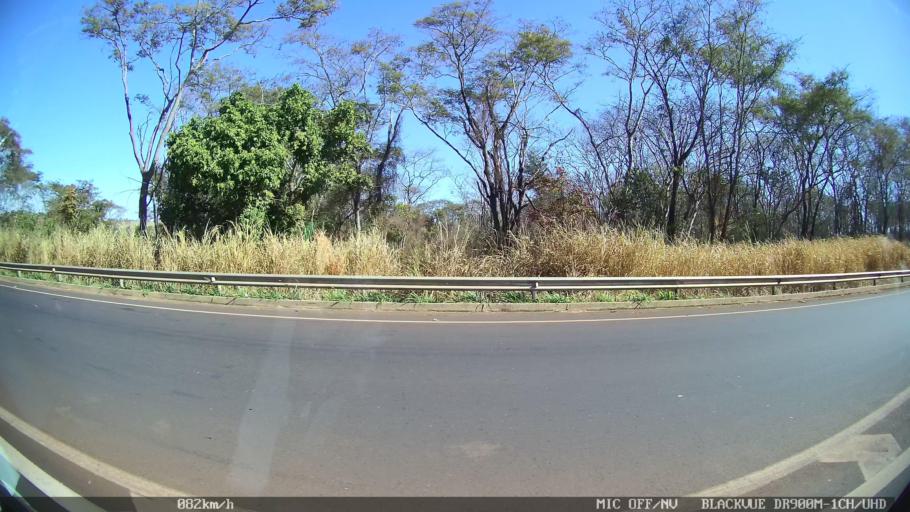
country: BR
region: Sao Paulo
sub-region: Olimpia
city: Olimpia
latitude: -20.6864
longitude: -48.9031
